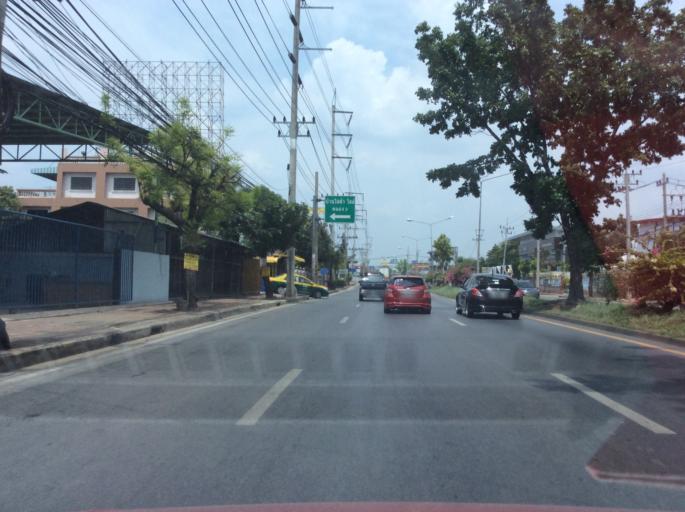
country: TH
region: Bangkok
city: Sai Mai
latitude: 13.9321
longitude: 100.6611
